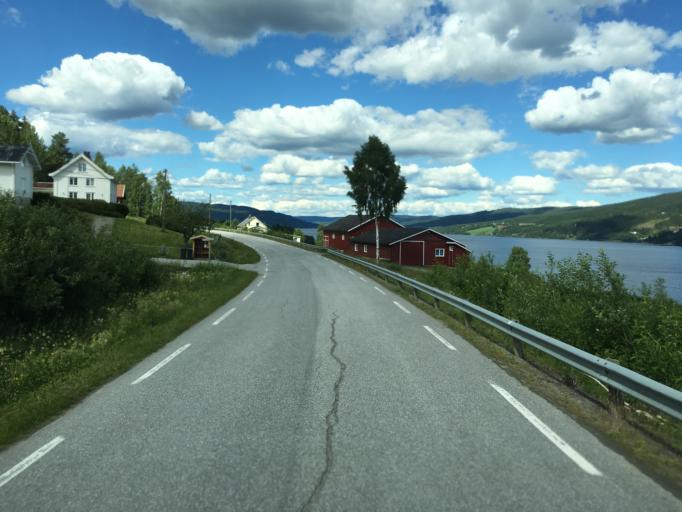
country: NO
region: Oppland
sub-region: Sondre Land
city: Hov
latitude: 60.5330
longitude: 10.2927
